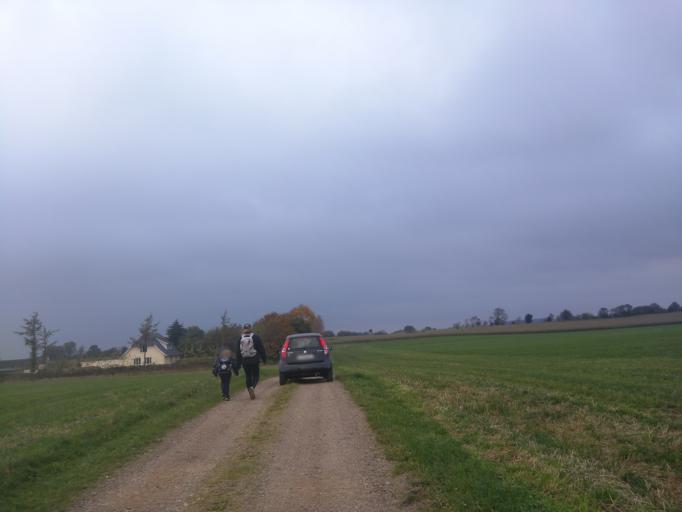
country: DK
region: Central Jutland
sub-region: Silkeborg Kommune
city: Silkeborg
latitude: 56.2470
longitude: 9.5171
